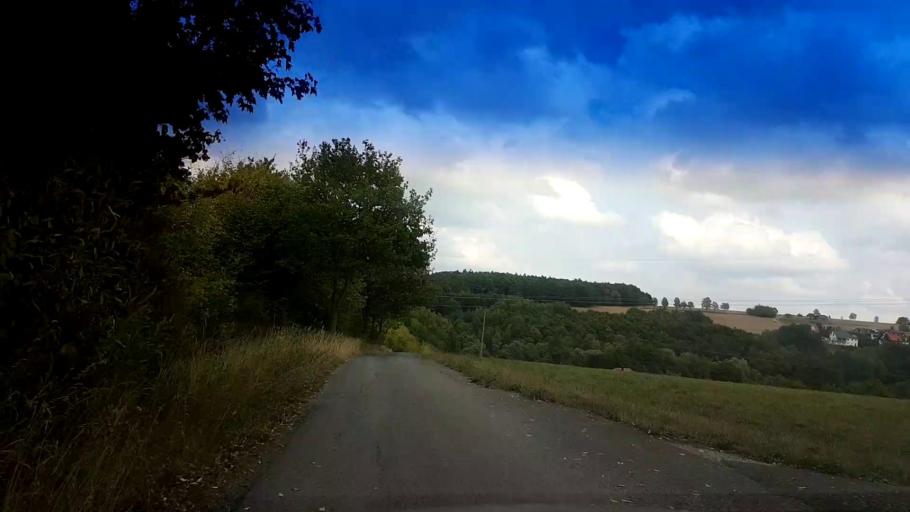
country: DE
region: Bavaria
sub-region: Upper Franconia
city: Zapfendorf
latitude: 50.0066
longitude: 10.9320
